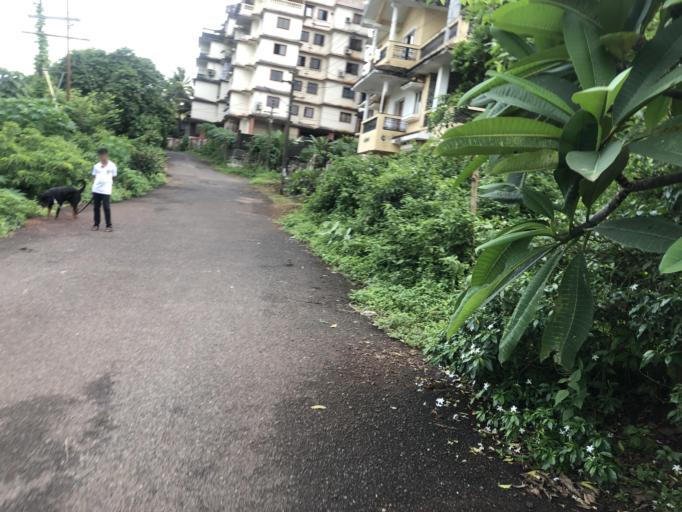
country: IN
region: Goa
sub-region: North Goa
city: Serula
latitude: 15.5466
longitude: 73.8257
